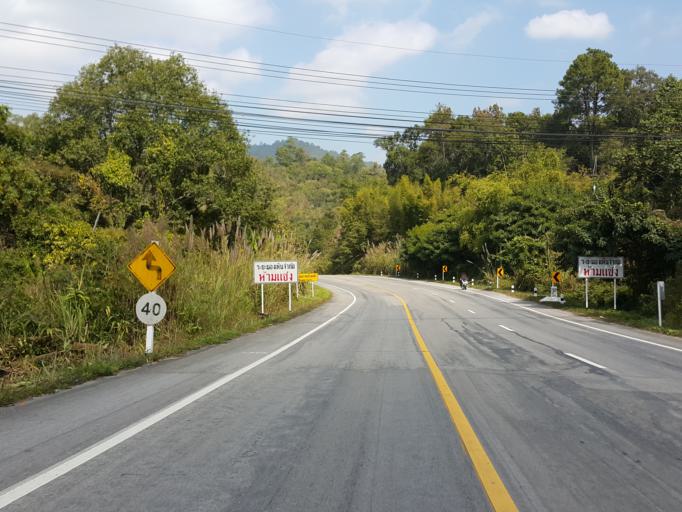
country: TH
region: Lampang
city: Wang Nuea
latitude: 19.0765
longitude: 99.3947
